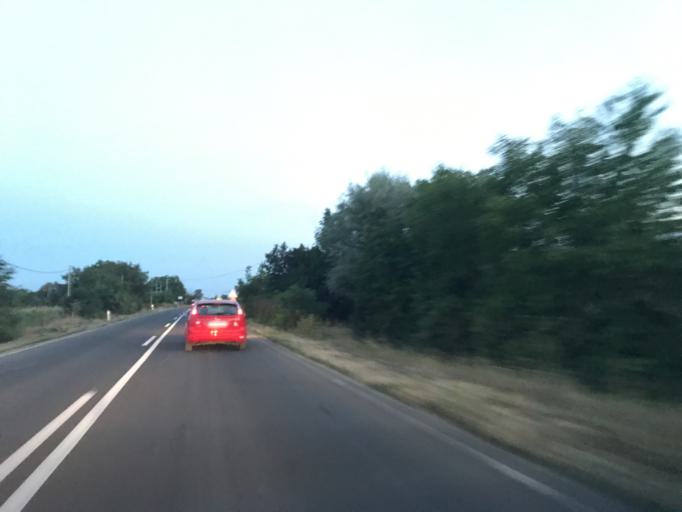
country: RS
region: Central Serbia
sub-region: Branicevski Okrug
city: Pozarevac
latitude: 44.6234
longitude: 21.1454
